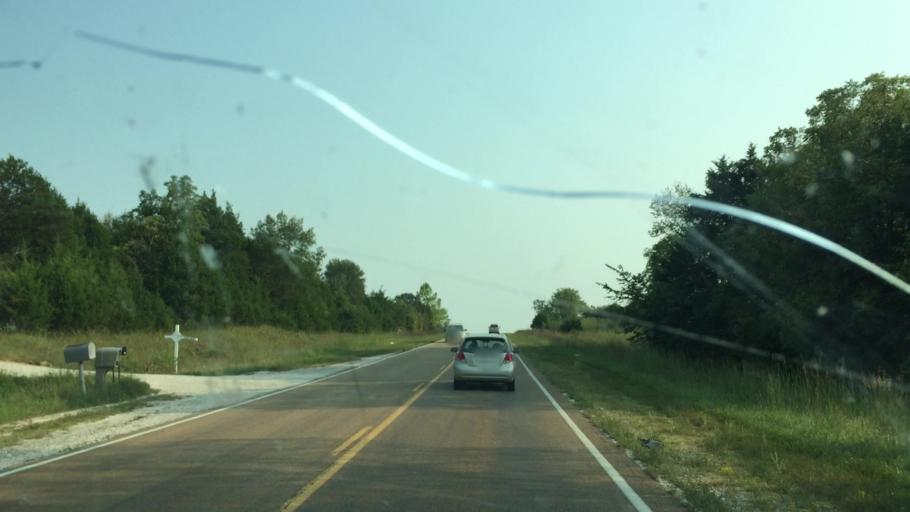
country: US
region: Missouri
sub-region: Pulaski County
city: Richland
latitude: 37.8334
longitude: -92.4065
